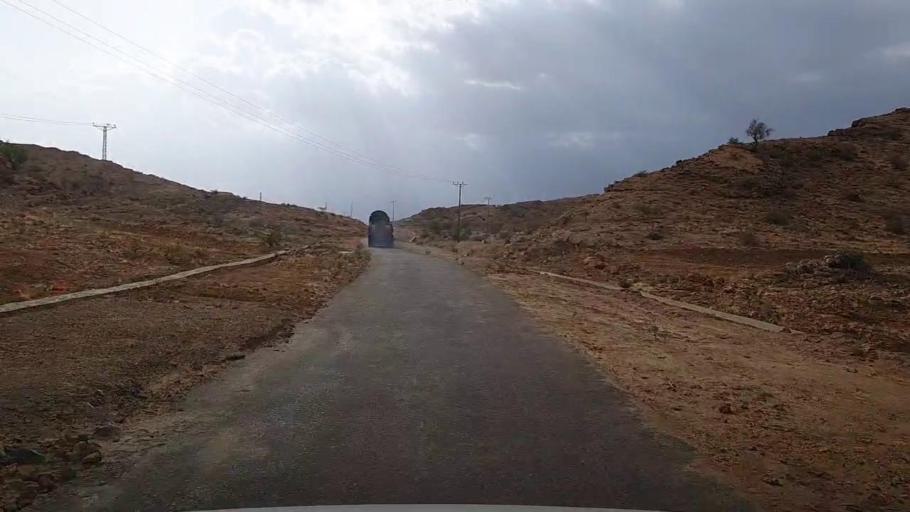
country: PK
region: Sindh
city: Jamshoro
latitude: 25.4975
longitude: 67.6445
